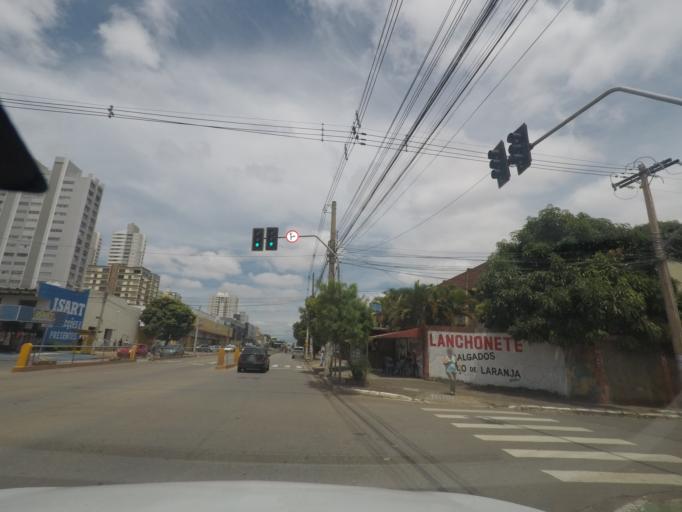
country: BR
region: Goias
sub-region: Goiania
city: Goiania
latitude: -16.6695
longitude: -49.2403
